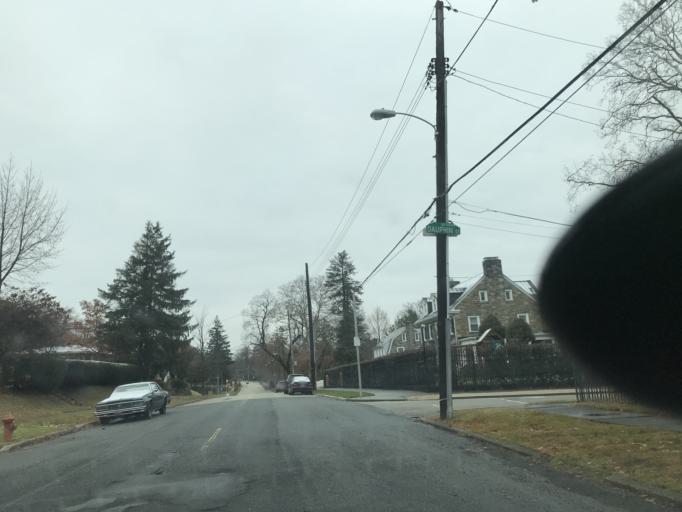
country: US
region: Pennsylvania
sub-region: Montgomery County
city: Bala-Cynwyd
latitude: 39.9924
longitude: -75.2301
